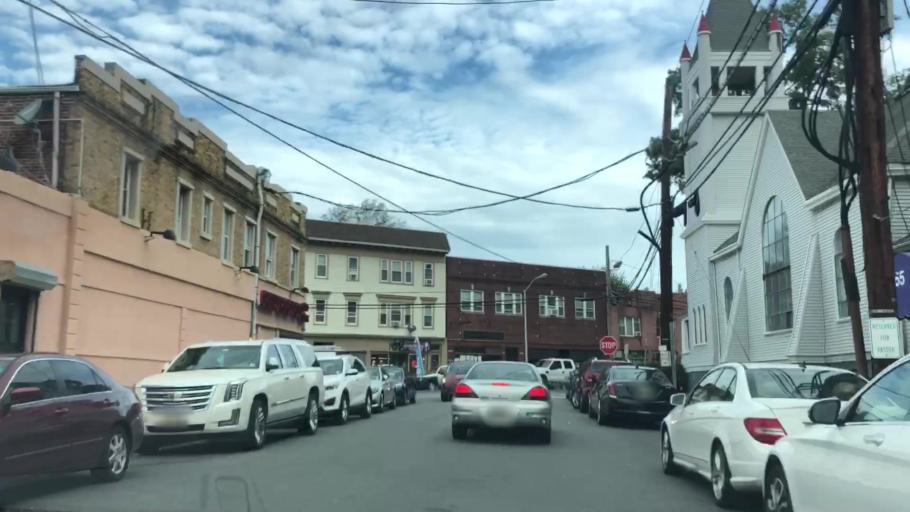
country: US
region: New Jersey
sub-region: Essex County
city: East Orange
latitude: 40.7820
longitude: -74.1999
